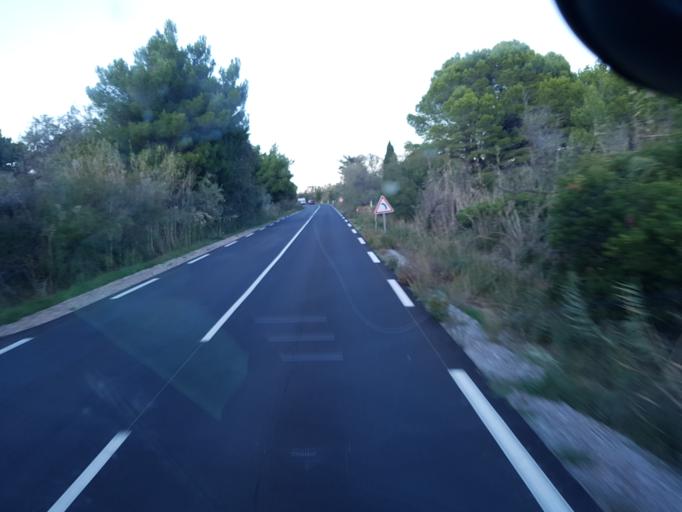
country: FR
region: Languedoc-Roussillon
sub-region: Departement de l'Aude
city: Port-la-Nouvelle
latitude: 42.9951
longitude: 3.0404
